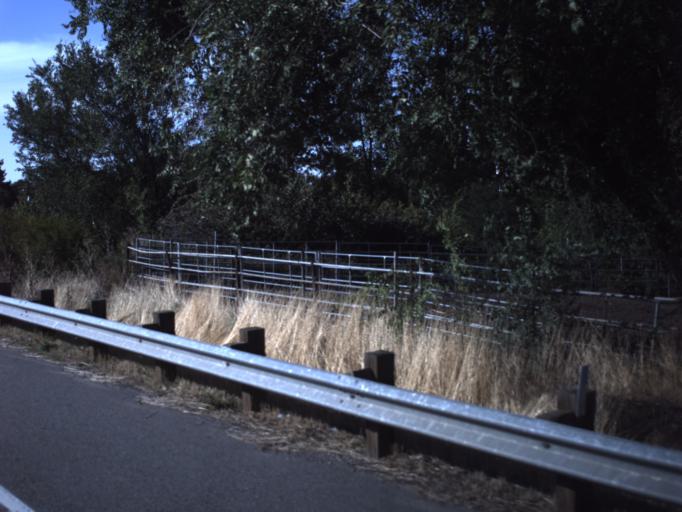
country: US
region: Utah
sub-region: Salt Lake County
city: Holladay
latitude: 40.6439
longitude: -111.8418
